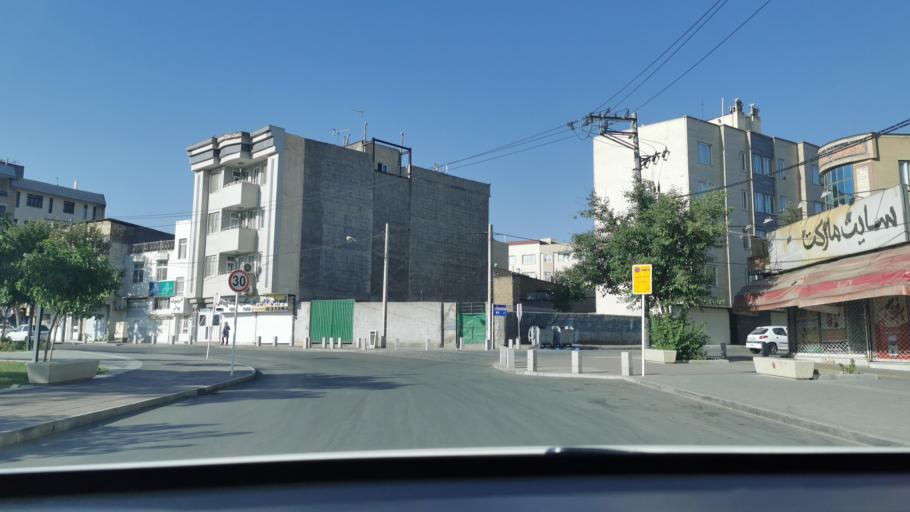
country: IR
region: Razavi Khorasan
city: Mashhad
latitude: 36.3109
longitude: 59.5108
